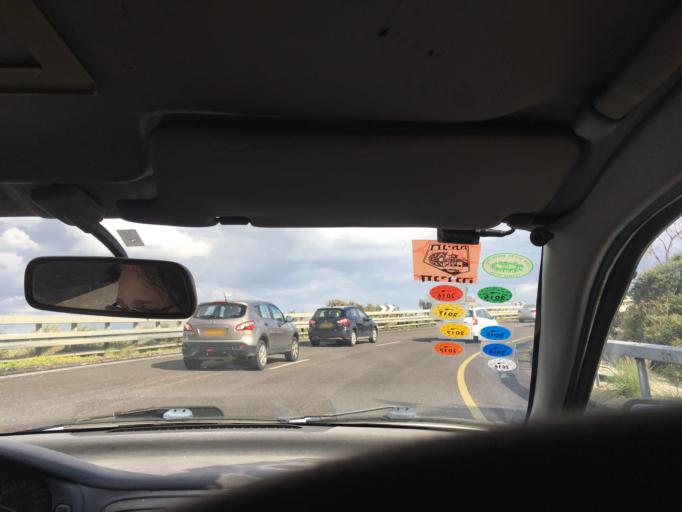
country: IL
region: Tel Aviv
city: Ramat HaSharon
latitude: 32.1396
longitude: 34.8103
